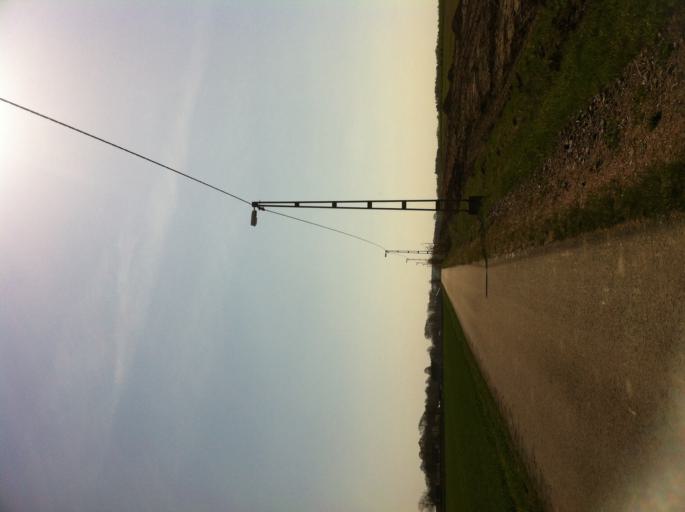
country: SE
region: Skane
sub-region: Kavlinge Kommun
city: Hofterup
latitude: 55.8310
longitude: 13.0075
